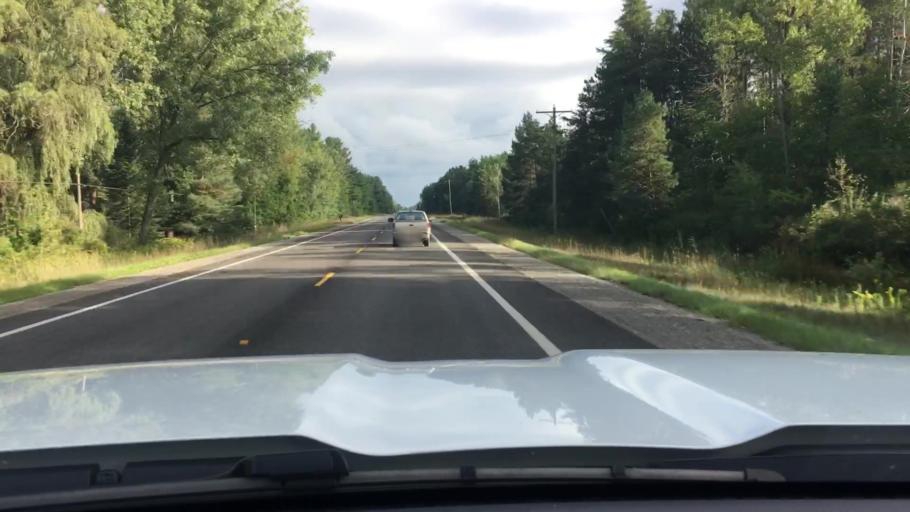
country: US
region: Michigan
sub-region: Tuscola County
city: Caro
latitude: 43.4251
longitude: -83.3845
